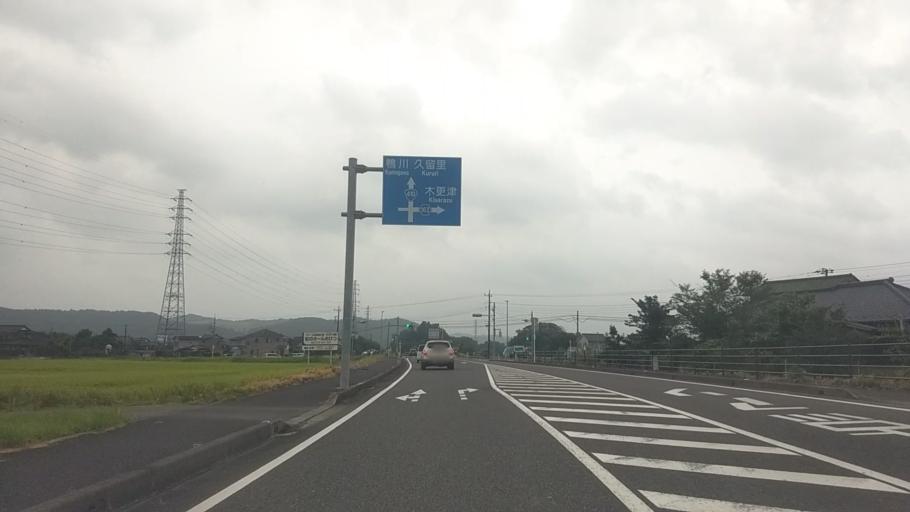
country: JP
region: Chiba
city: Kisarazu
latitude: 35.3144
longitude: 140.0555
